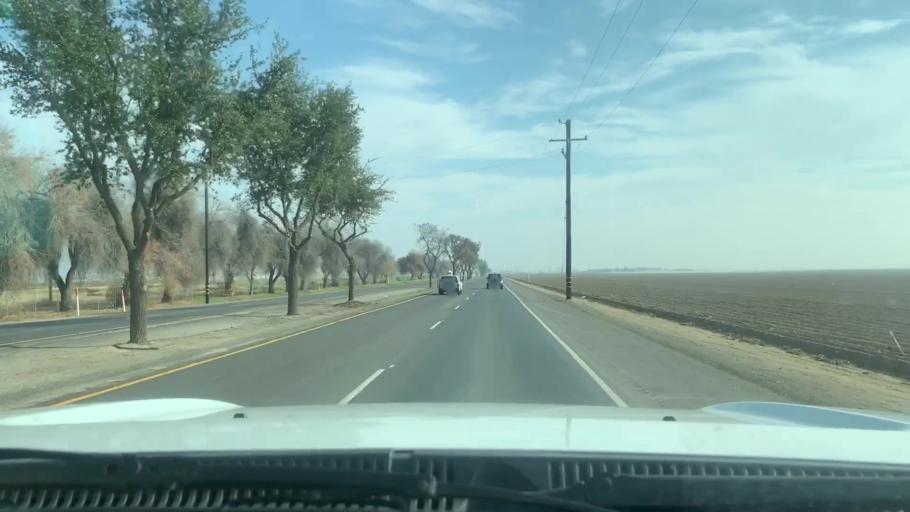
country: US
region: California
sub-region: Kern County
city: Shafter
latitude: 35.4997
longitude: -119.2052
